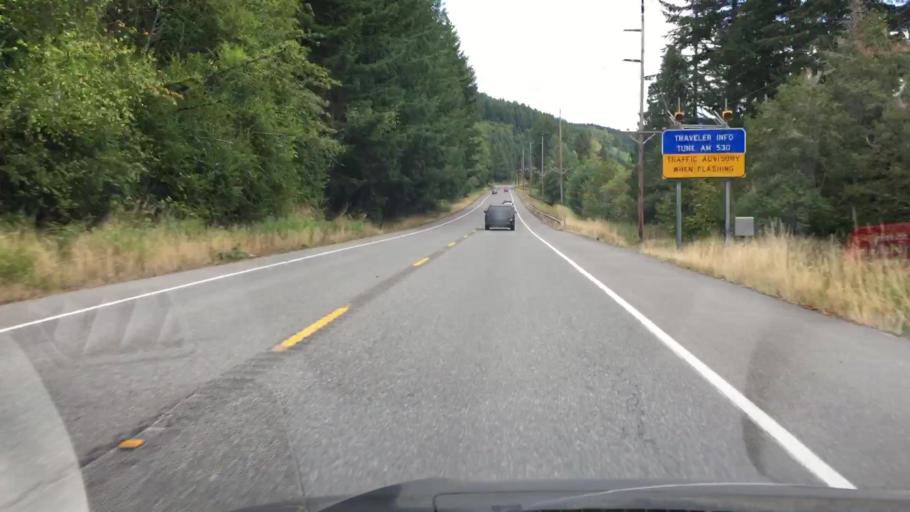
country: US
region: Washington
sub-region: Pierce County
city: Eatonville
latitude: 46.7821
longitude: -122.2398
